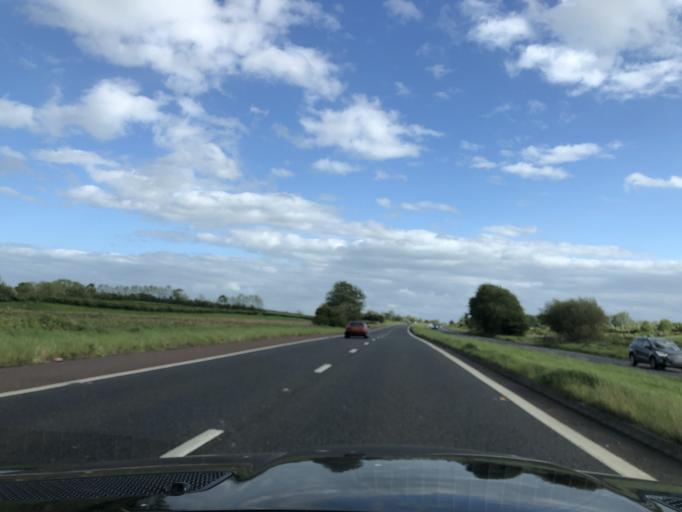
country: GB
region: Northern Ireland
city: Cullybackey
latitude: 54.9275
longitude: -6.3248
